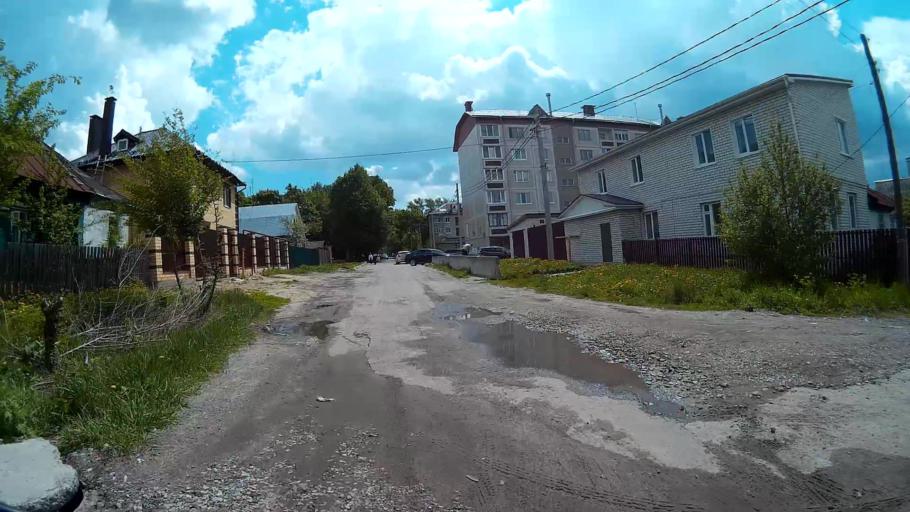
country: RU
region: Ulyanovsk
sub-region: Ulyanovskiy Rayon
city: Ulyanovsk
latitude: 54.3426
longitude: 48.3680
